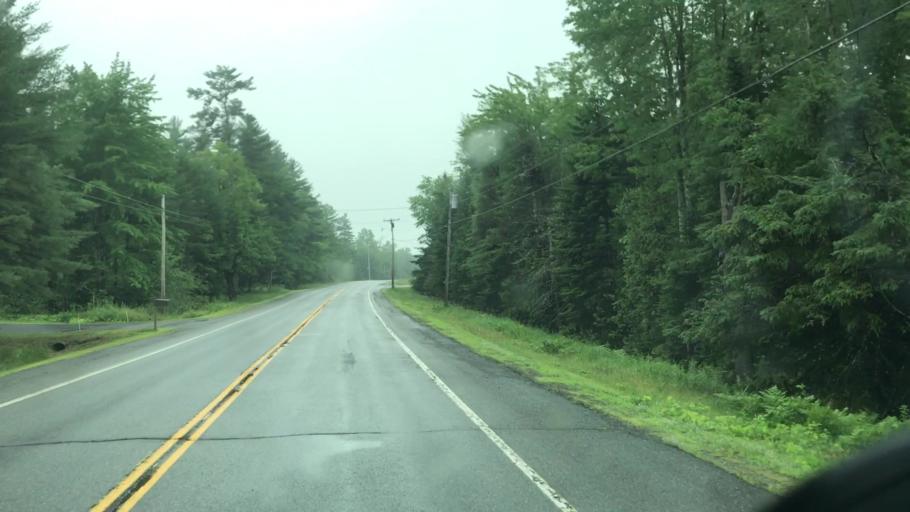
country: US
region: Maine
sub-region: Penobscot County
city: Howland
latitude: 45.2537
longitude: -68.6376
